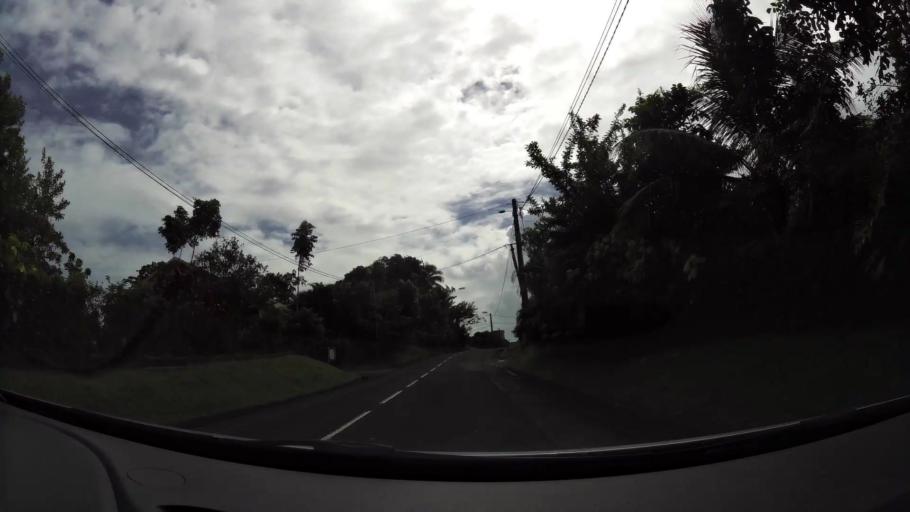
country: MQ
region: Martinique
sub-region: Martinique
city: Saint-Joseph
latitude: 14.6422
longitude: -61.0427
